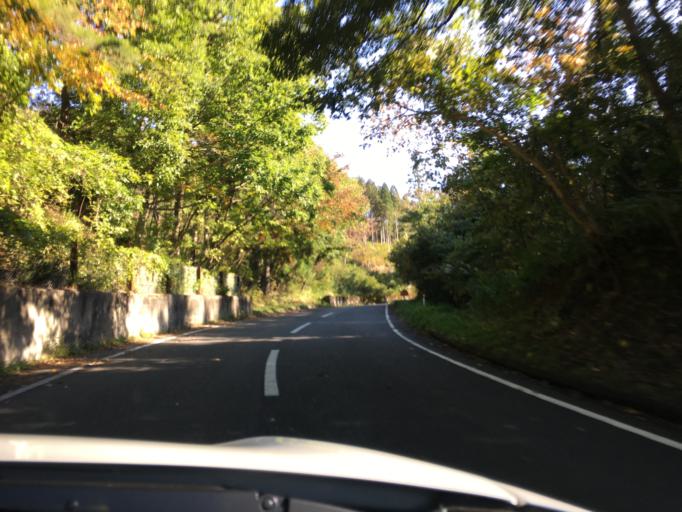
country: JP
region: Fukushima
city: Ishikawa
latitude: 37.1594
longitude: 140.5994
